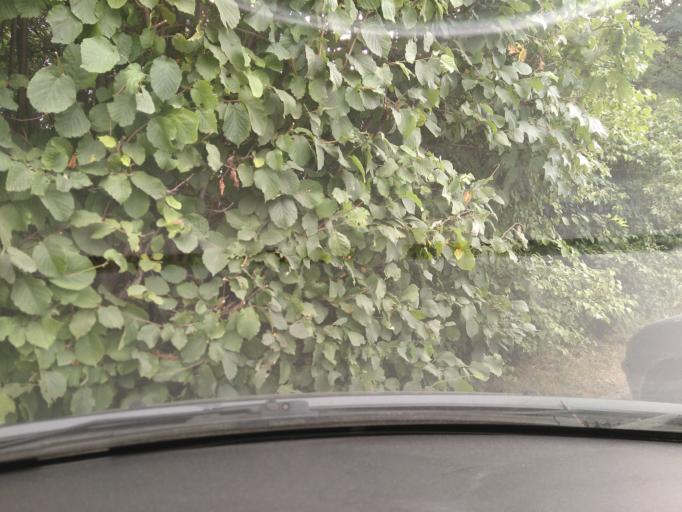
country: FR
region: Rhone-Alpes
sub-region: Departement de l'Isere
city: Vaulnaveys-le-Haut
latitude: 45.1463
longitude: 5.8339
